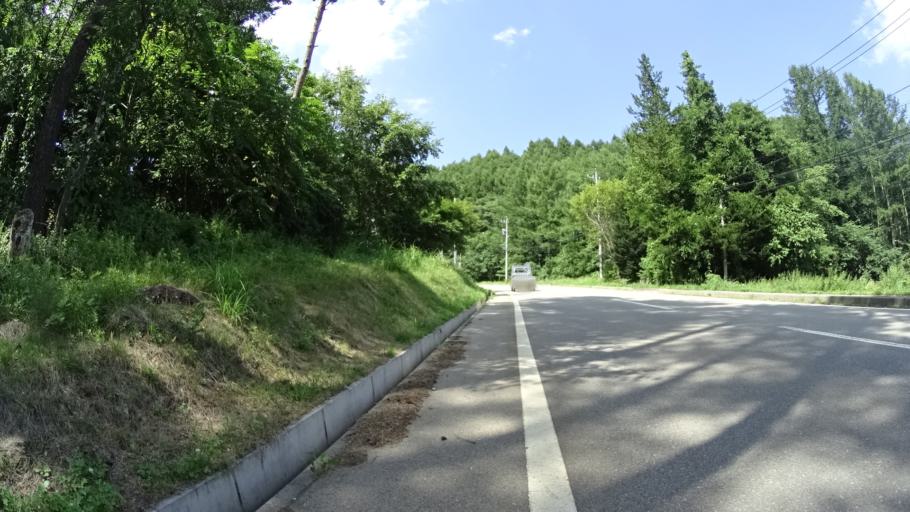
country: JP
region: Nagano
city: Saku
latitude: 36.0542
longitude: 138.4508
